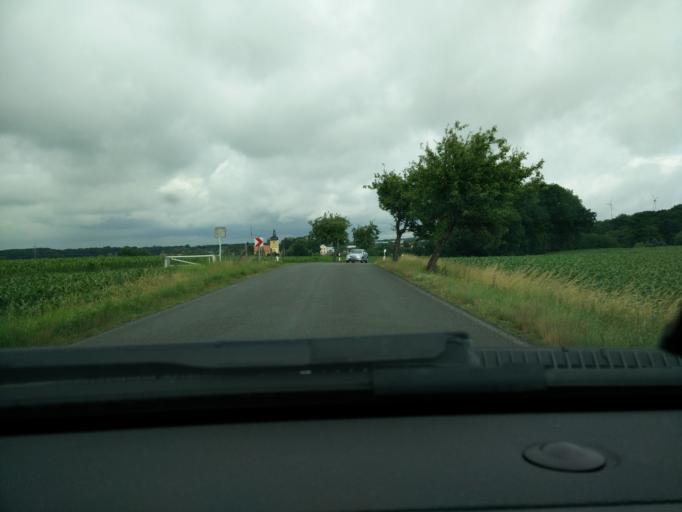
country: DE
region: Saxony
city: Geithain
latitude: 51.0831
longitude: 12.6898
